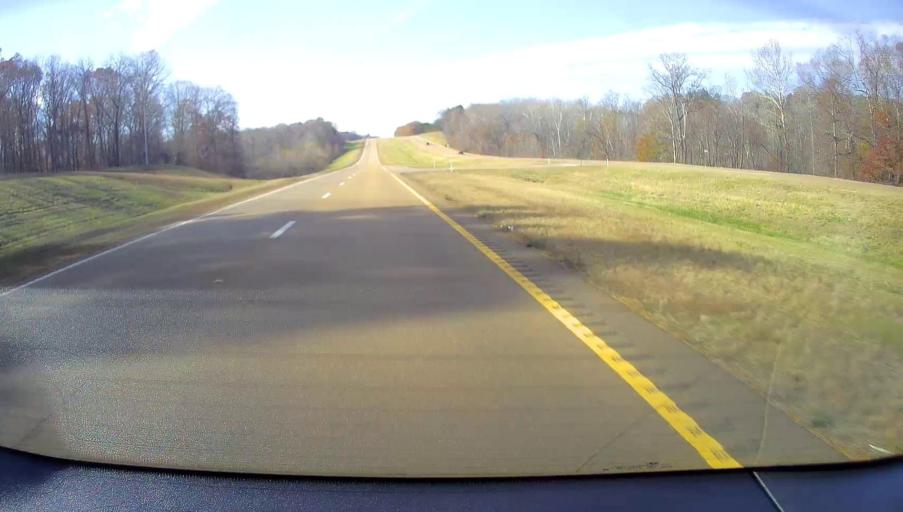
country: US
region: Mississippi
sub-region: Benton County
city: Ashland
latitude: 34.9469
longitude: -89.1249
